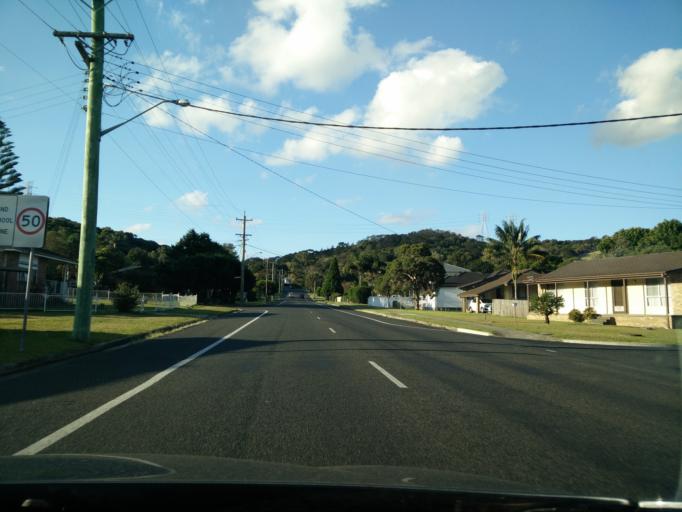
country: AU
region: New South Wales
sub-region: Wollongong
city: Berkeley
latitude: -34.4740
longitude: 150.8416
